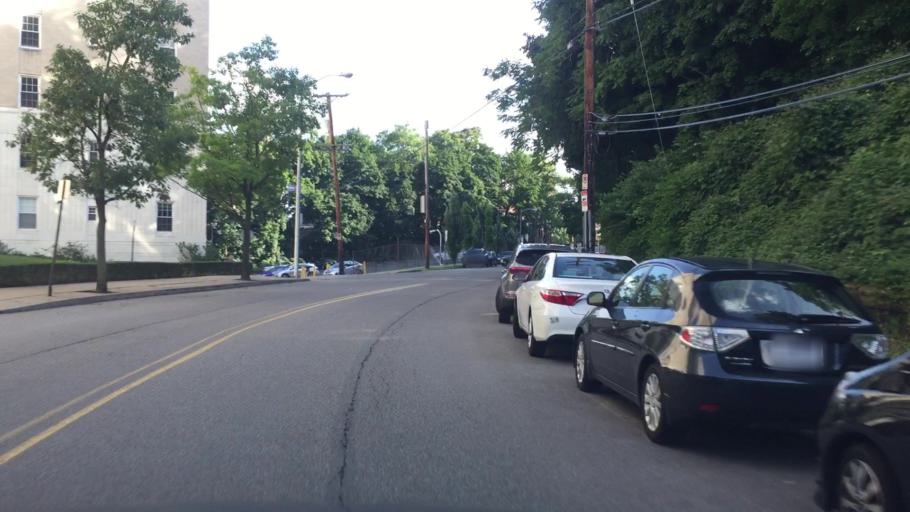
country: US
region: Pennsylvania
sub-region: Allegheny County
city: Bloomfield
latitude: 40.4532
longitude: -79.9541
